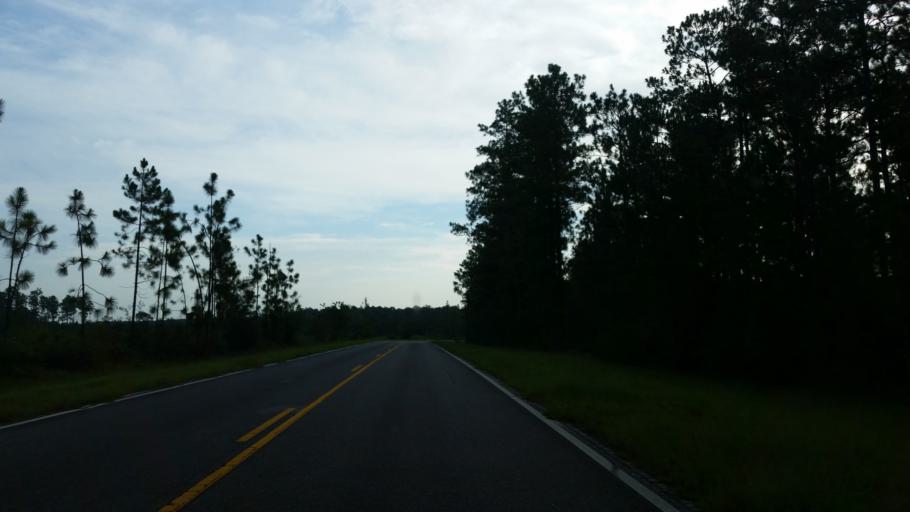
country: US
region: Florida
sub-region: Escambia County
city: Molino
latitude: 30.7727
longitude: -87.4975
